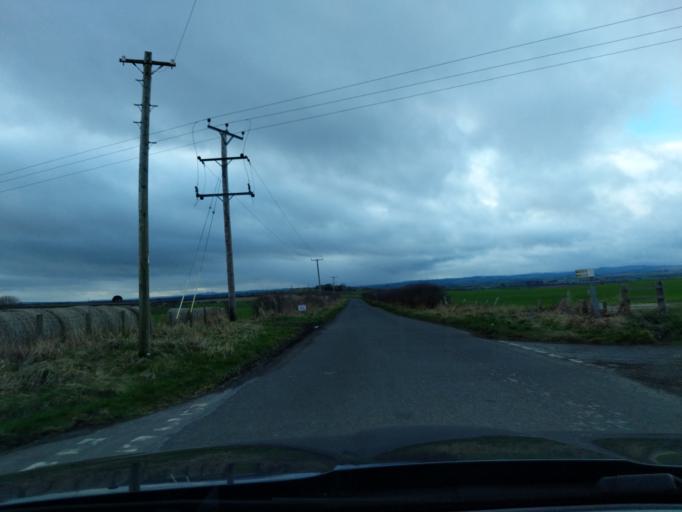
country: GB
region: England
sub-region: Northumberland
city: Ancroft
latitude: 55.7133
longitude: -2.0720
